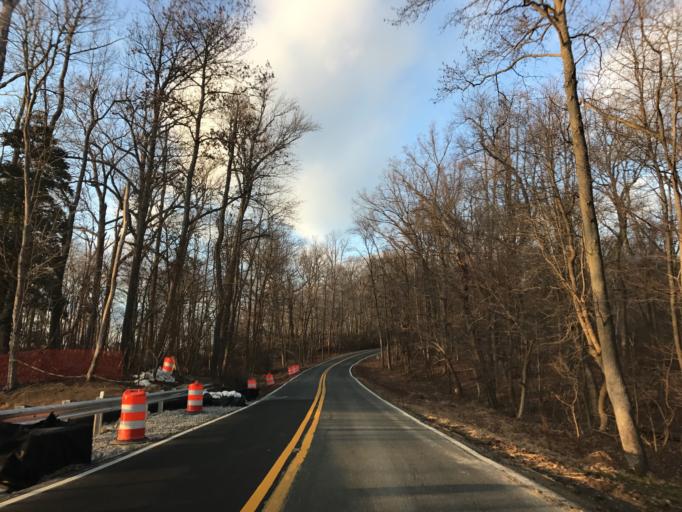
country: US
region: Maryland
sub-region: Cecil County
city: Charlestown
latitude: 39.4751
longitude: -75.9923
